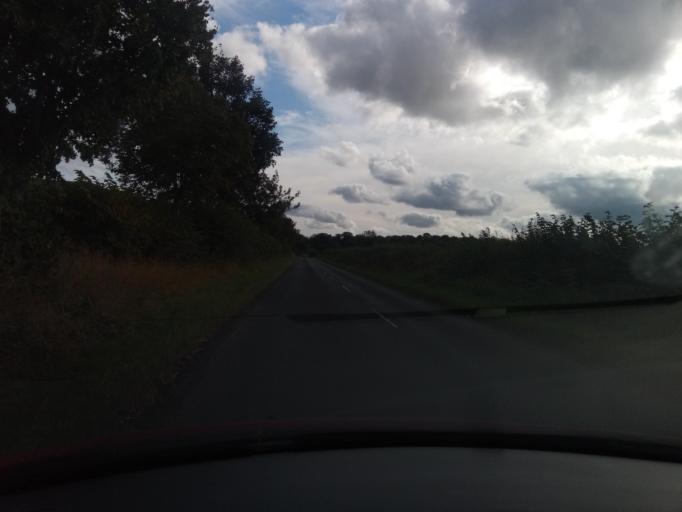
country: GB
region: Scotland
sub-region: The Scottish Borders
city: Kelso
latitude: 55.5259
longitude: -2.3578
